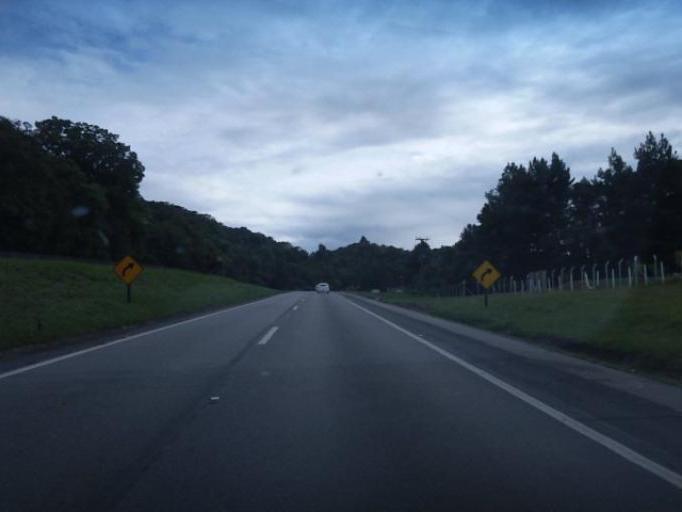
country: BR
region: Parana
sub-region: Campina Grande Do Sul
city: Campina Grande do Sul
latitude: -25.1716
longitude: -48.8676
